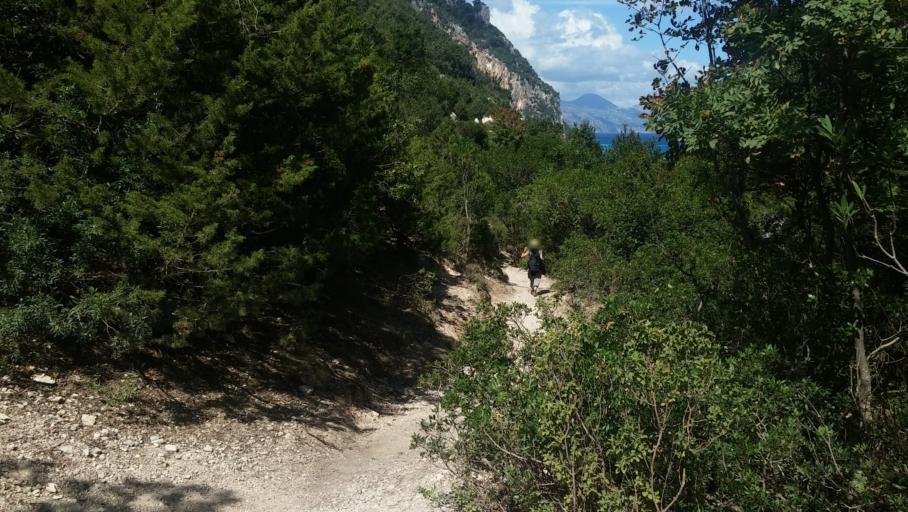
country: IT
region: Sardinia
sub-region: Provincia di Ogliastra
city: Baunei
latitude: 40.1068
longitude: 9.6900
